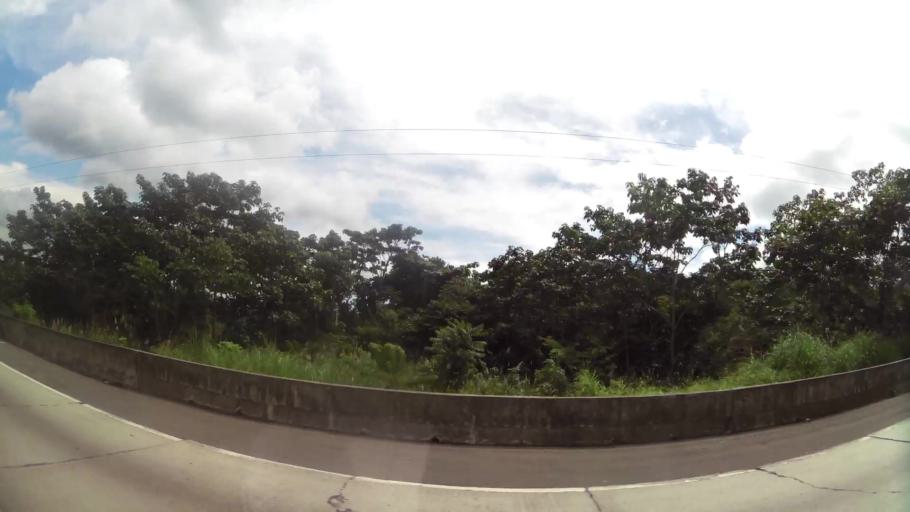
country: PA
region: Panama
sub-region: Distrito de Panama
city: Paraiso
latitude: 9.0102
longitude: -79.6466
